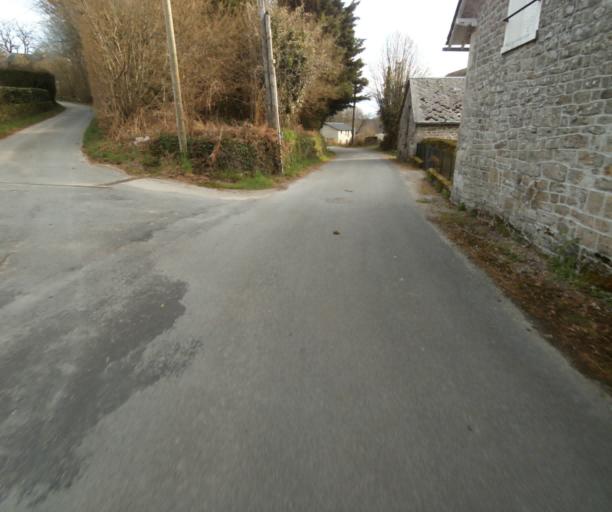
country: FR
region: Limousin
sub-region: Departement de la Correze
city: Correze
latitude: 45.4041
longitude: 1.9007
